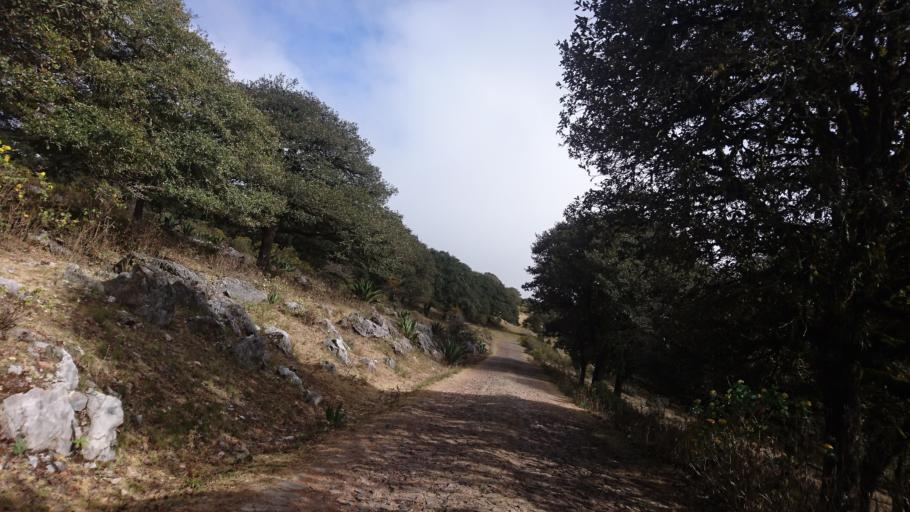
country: MX
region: San Luis Potosi
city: Zaragoza
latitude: 22.0672
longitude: -100.6445
